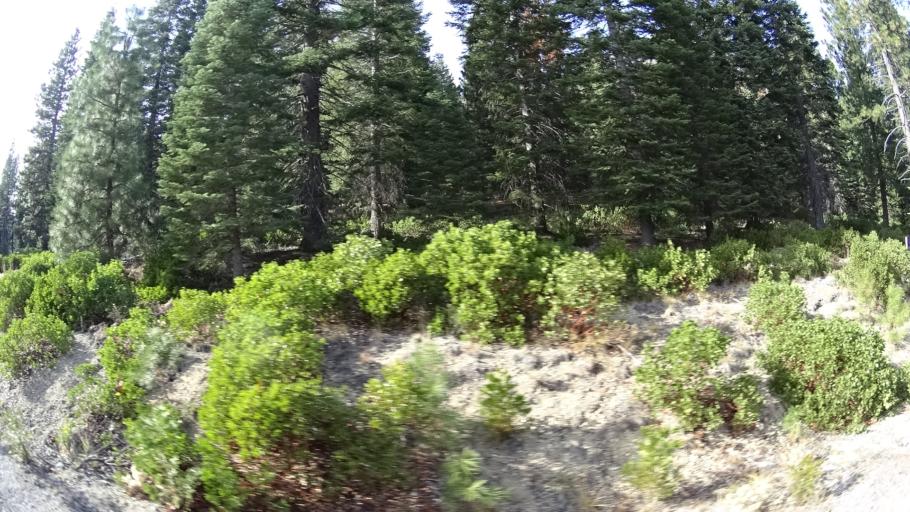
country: US
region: California
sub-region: Siskiyou County
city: Weed
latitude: 41.3932
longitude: -122.3909
